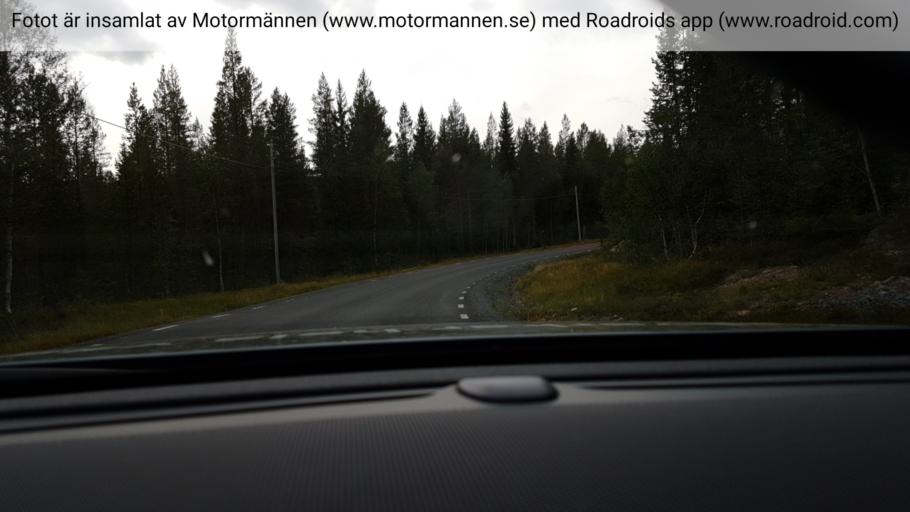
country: NO
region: Hedmark
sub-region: Trysil
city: Innbygda
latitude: 61.6549
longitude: 12.7289
